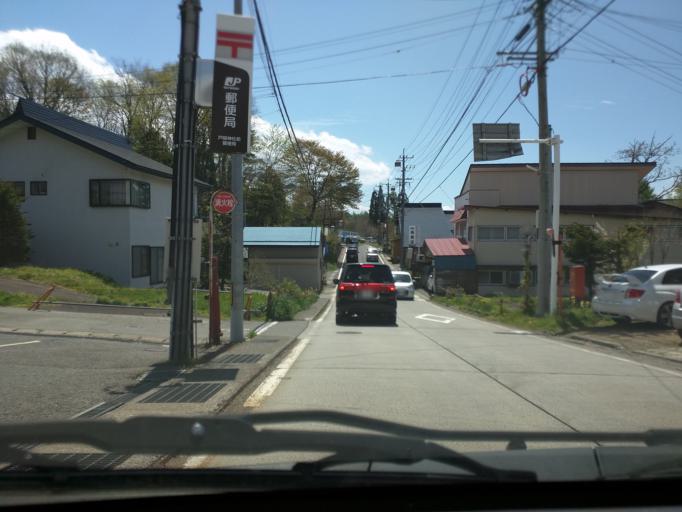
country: JP
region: Nagano
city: Nagano-shi
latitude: 36.7286
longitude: 138.0773
